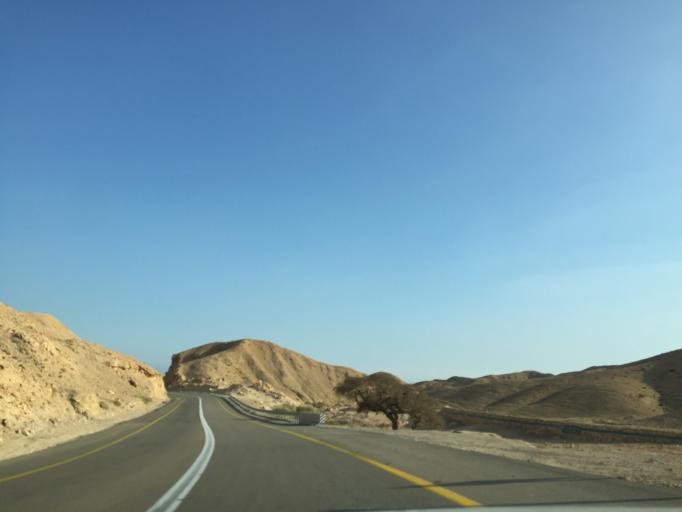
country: IL
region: Southern District
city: `En Boqeq
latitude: 31.1915
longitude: 35.2807
